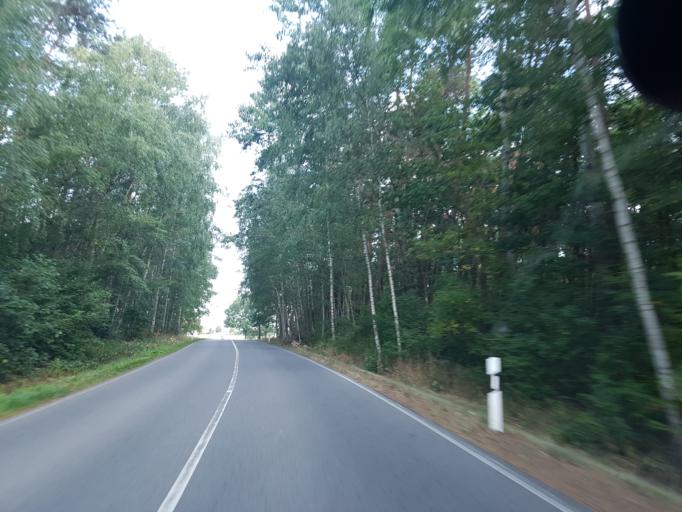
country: DE
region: Brandenburg
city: Sonnewalde
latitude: 51.6761
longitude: 13.6888
